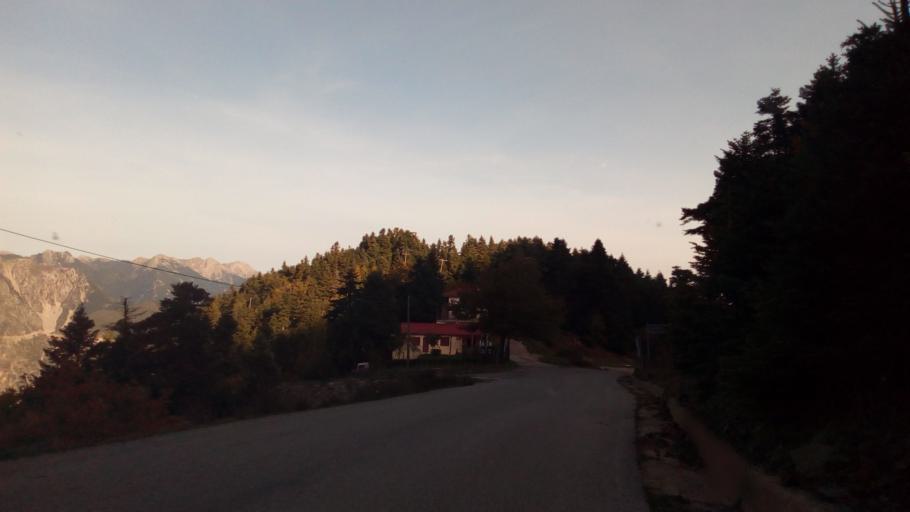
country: GR
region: West Greece
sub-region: Nomos Aitolias kai Akarnanias
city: Thermo
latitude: 38.6355
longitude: 21.8356
